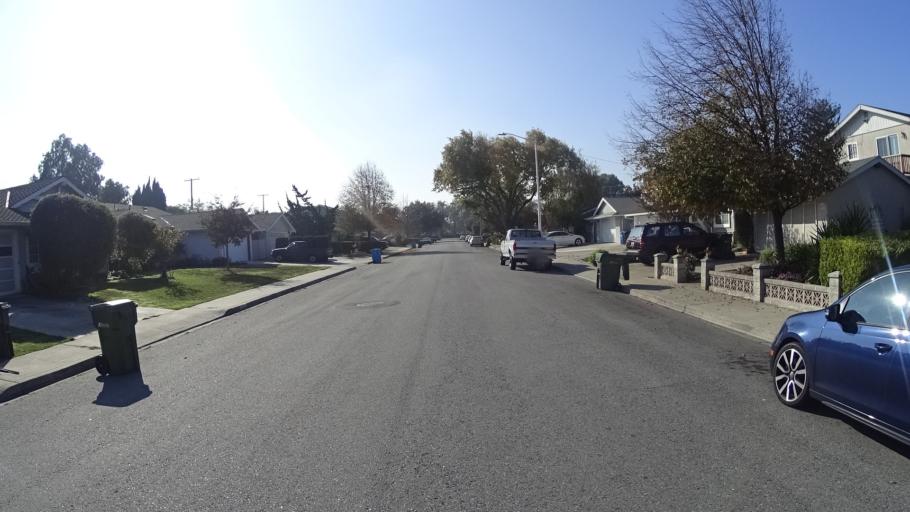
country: US
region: California
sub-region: Santa Clara County
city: Santa Clara
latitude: 37.3582
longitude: -121.9810
